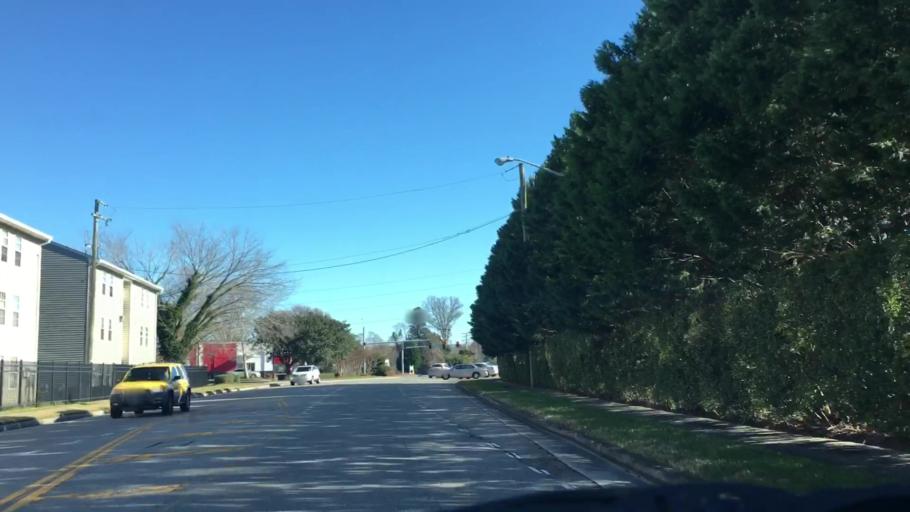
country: US
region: Virginia
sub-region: City of Virginia Beach
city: Virginia Beach
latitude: 36.8526
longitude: -76.0247
